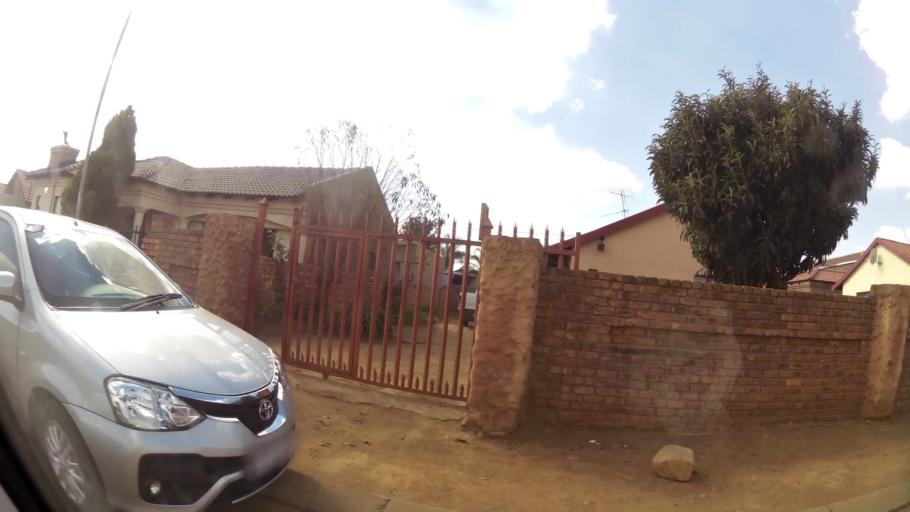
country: ZA
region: Gauteng
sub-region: City of Tshwane Metropolitan Municipality
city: Cullinan
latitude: -25.7005
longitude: 28.4070
